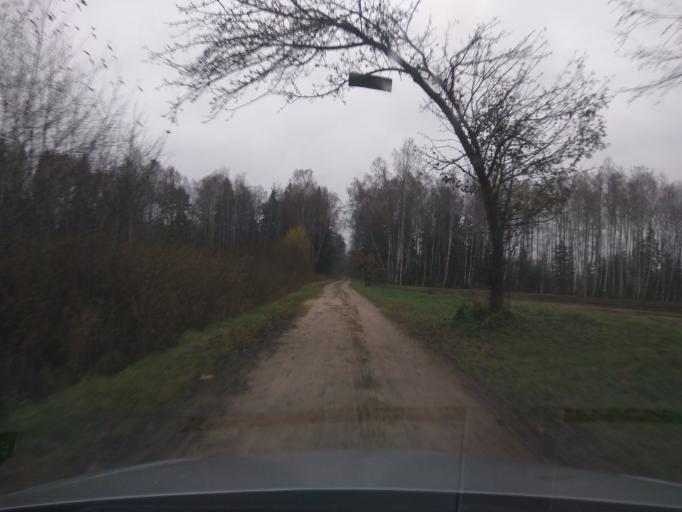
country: LV
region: Kuldigas Rajons
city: Kuldiga
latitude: 56.9250
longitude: 21.9734
